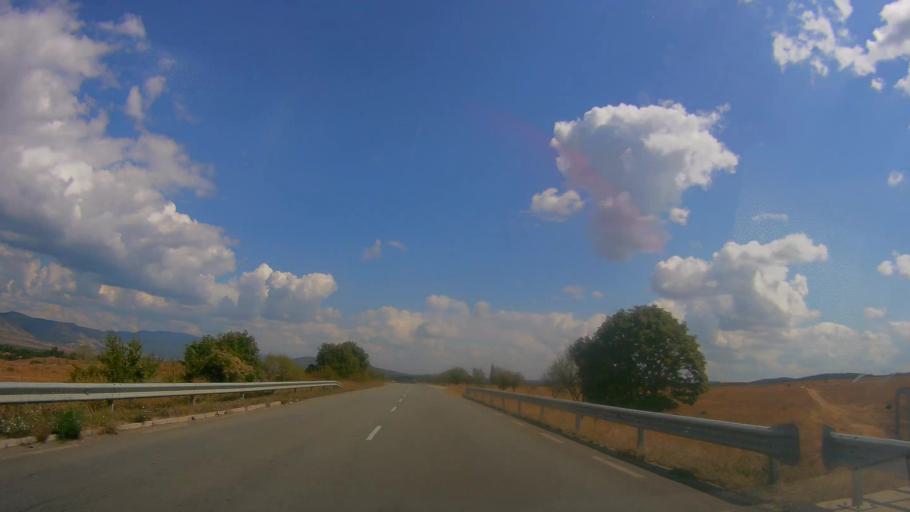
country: BG
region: Sliven
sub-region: Obshtina Tvurditsa
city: Tvurditsa
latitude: 42.6547
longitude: 25.9416
